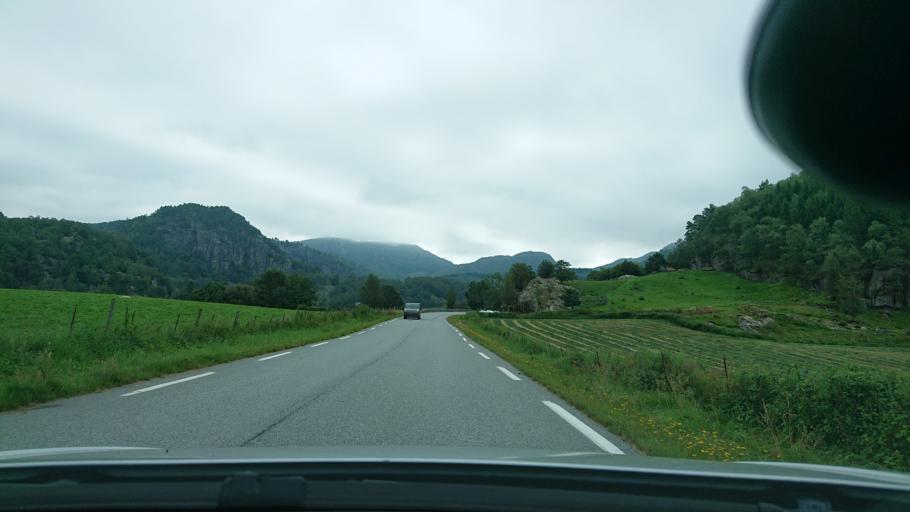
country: NO
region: Rogaland
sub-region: Hjelmeland
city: Hjelmelandsvagen
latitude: 59.2259
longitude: 6.2080
